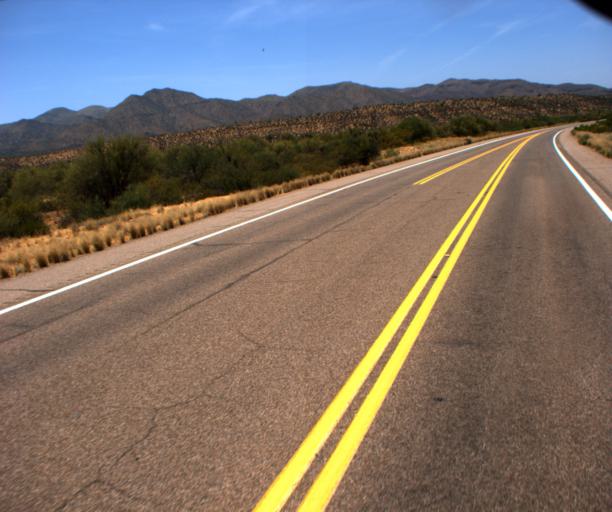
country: US
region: Arizona
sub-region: Gila County
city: Miami
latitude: 33.6183
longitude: -111.0533
